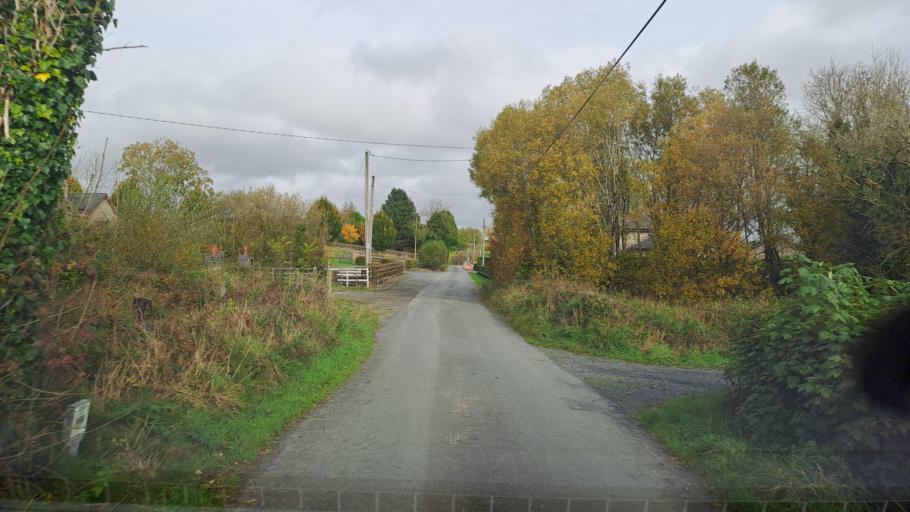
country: IE
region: Ulster
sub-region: County Monaghan
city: Carrickmacross
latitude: 53.9975
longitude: -6.7829
